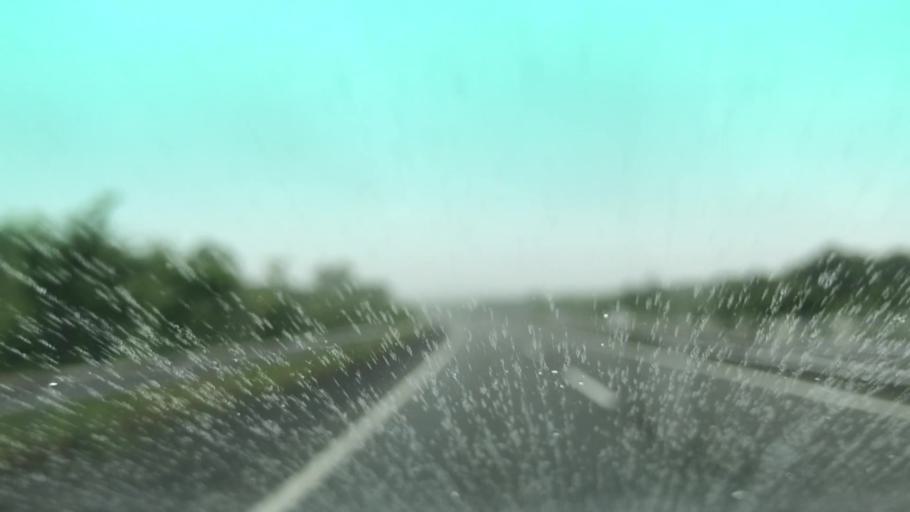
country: JP
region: Hokkaido
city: Shiraoi
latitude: 42.5370
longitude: 141.2746
